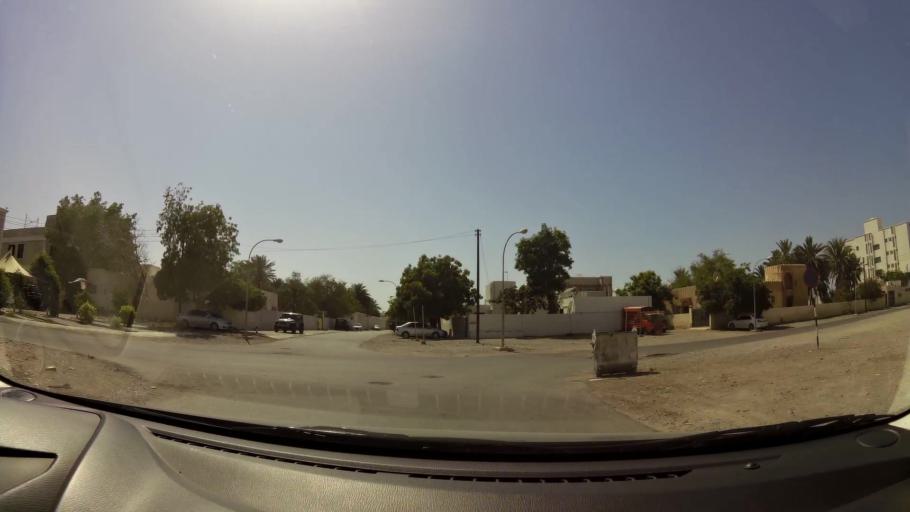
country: OM
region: Muhafazat Masqat
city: As Sib al Jadidah
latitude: 23.6409
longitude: 58.2223
